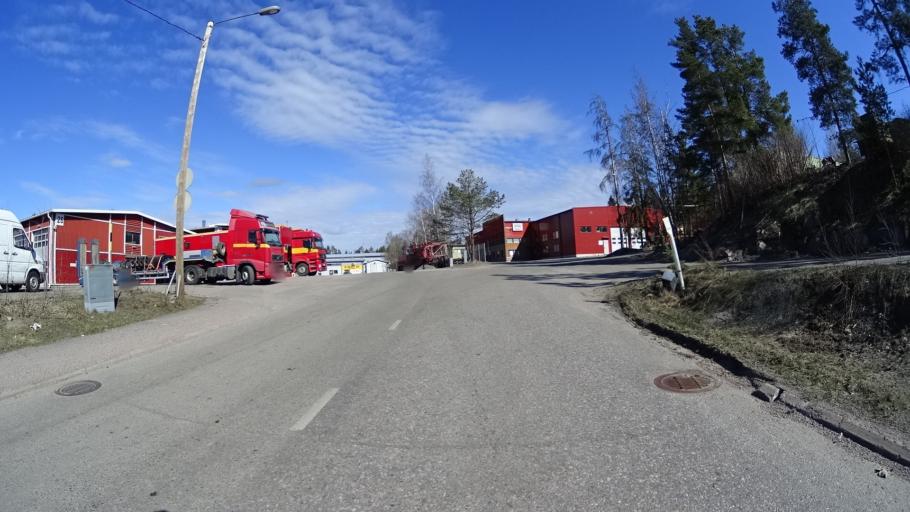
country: FI
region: Uusimaa
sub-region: Helsinki
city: Kilo
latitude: 60.2836
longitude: 24.7591
